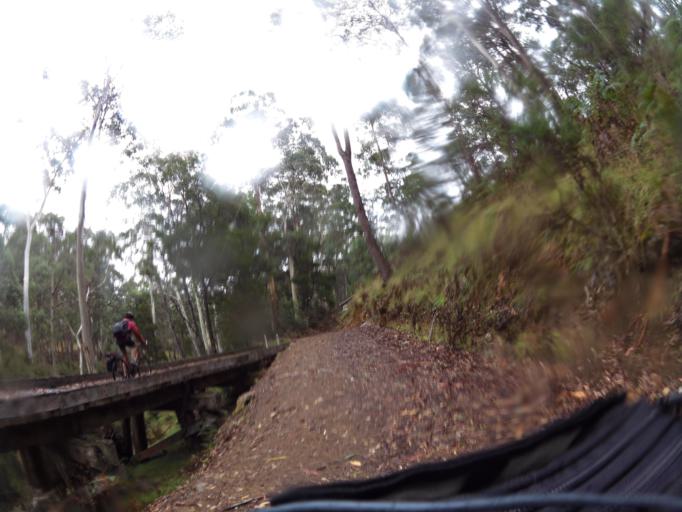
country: AU
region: New South Wales
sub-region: Greater Hume Shire
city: Holbrook
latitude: -36.1673
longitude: 147.4857
